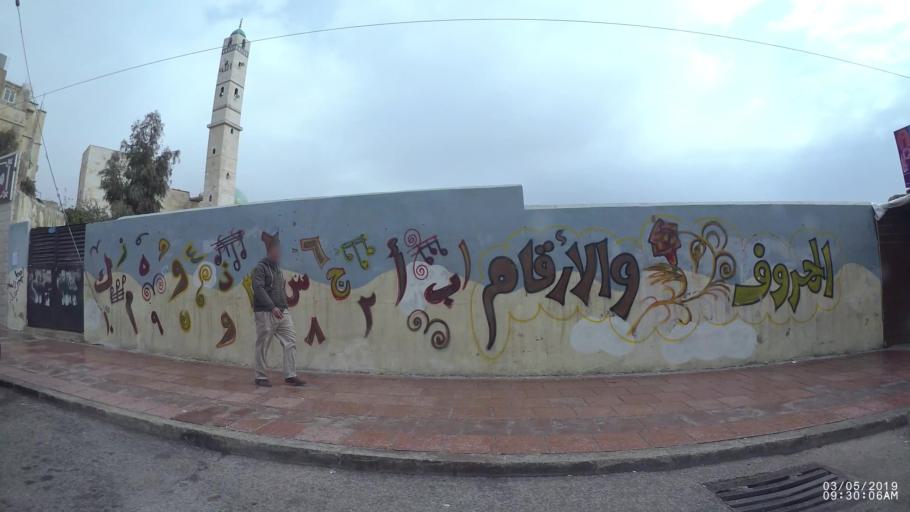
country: JO
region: Amman
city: Amman
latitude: 31.9735
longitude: 35.9267
